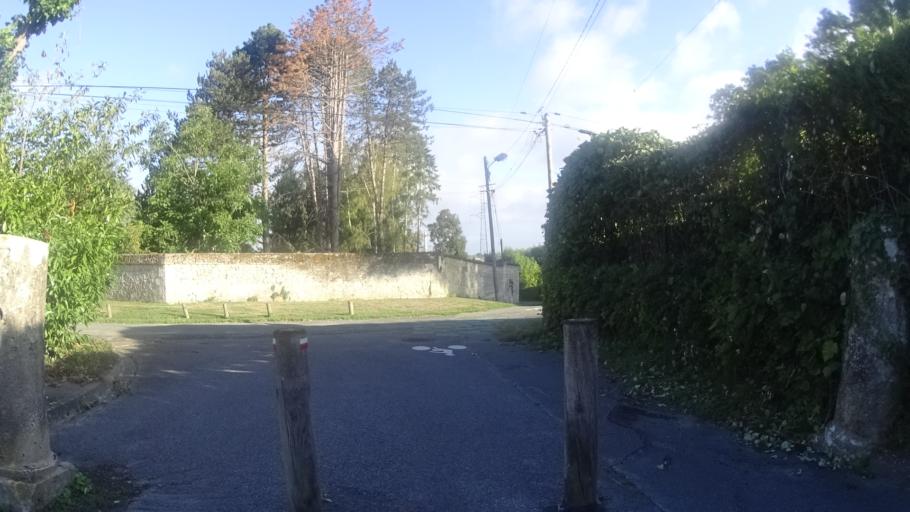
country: FR
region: Picardie
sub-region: Departement de l'Oise
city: Verberie
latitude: 49.3092
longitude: 2.7190
